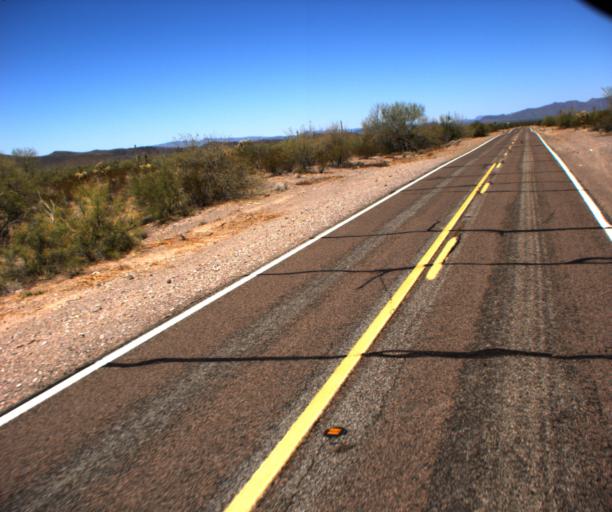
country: US
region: Arizona
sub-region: Pima County
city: Ajo
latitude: 32.2256
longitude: -112.7044
